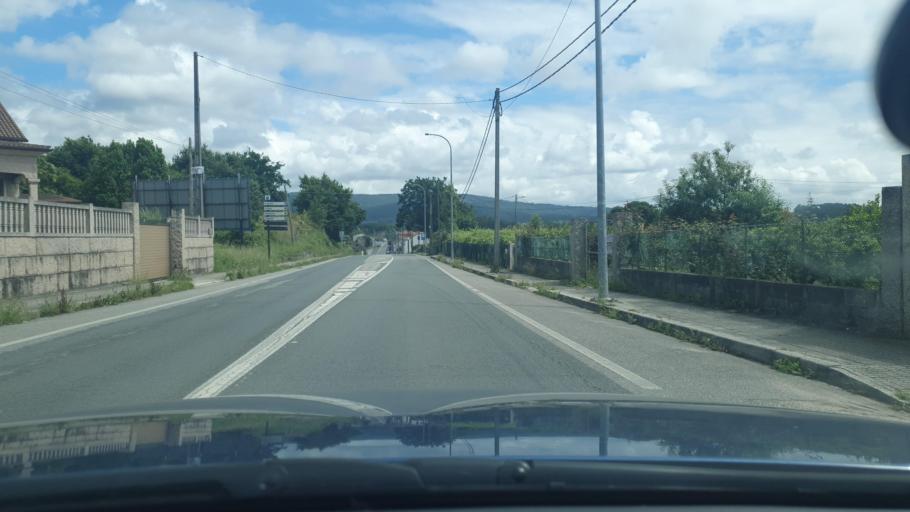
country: ES
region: Galicia
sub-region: Provincia de Pontevedra
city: Cambados
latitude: 42.5048
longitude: -8.8100
